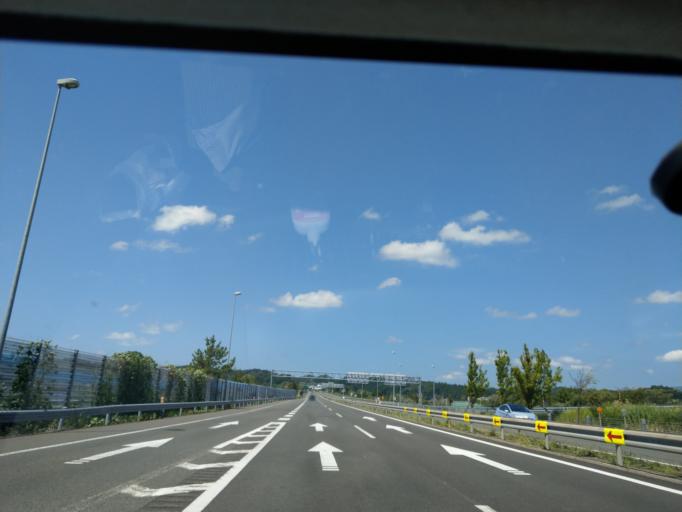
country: JP
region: Akita
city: Akita
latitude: 39.6431
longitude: 140.2098
